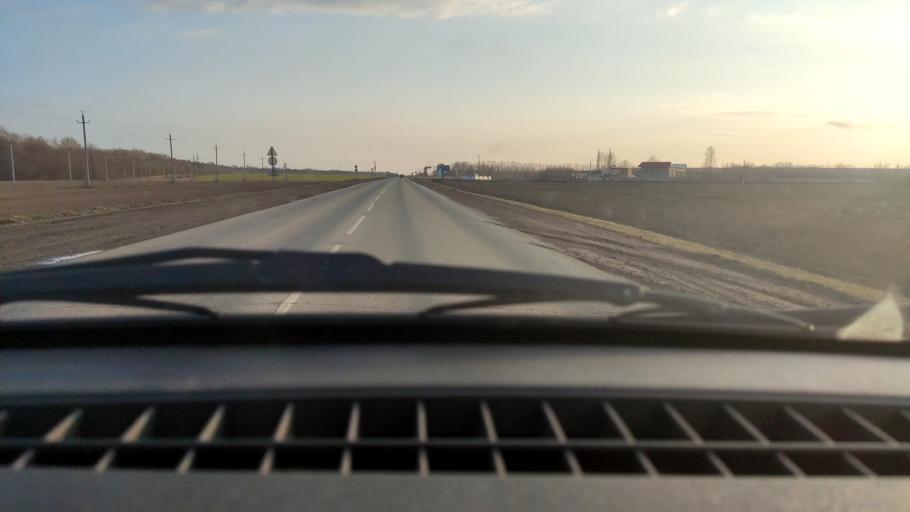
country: RU
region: Bashkortostan
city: Chishmy
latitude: 54.5704
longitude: 55.3541
